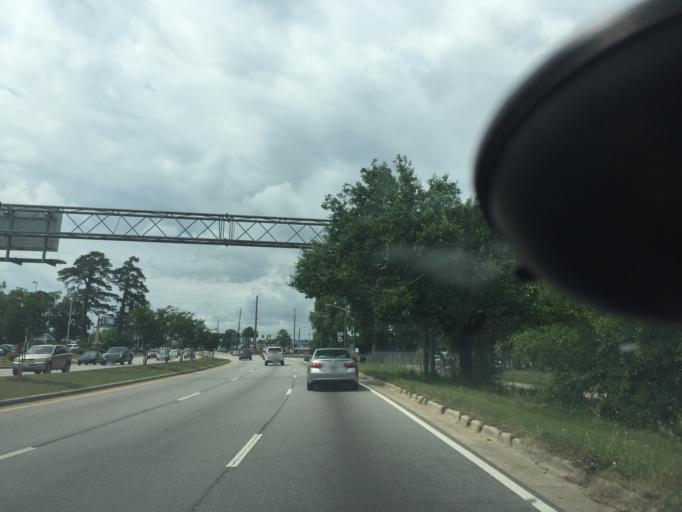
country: US
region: Georgia
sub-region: Chatham County
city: Montgomery
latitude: 32.0012
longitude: -81.1265
